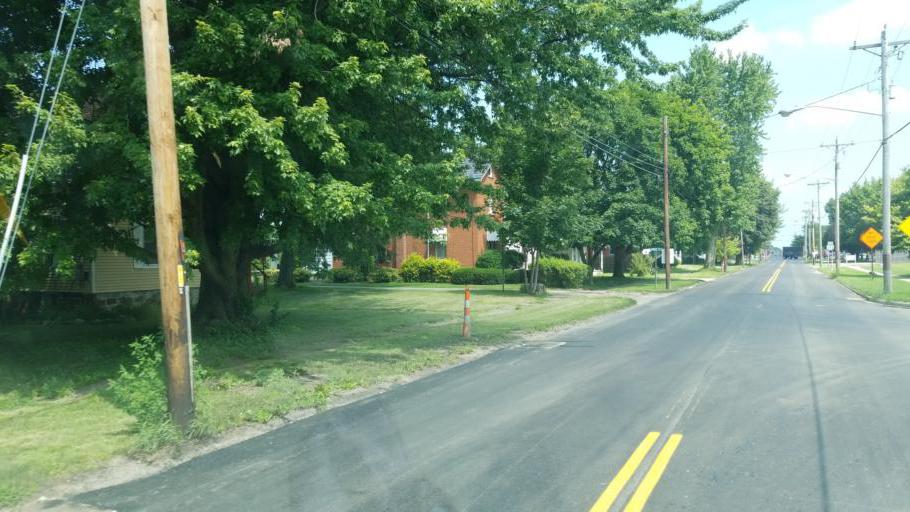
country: US
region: Ohio
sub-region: Huron County
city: Willard
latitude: 40.9590
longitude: -82.8536
